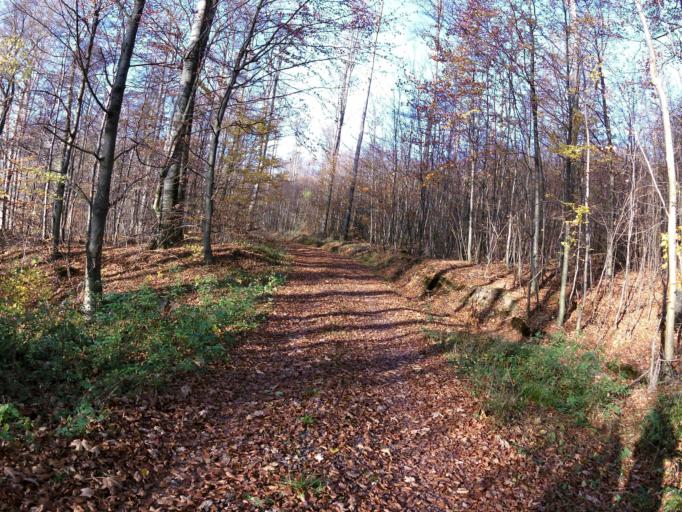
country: DE
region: Thuringia
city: Ruhla
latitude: 50.8760
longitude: 10.3948
